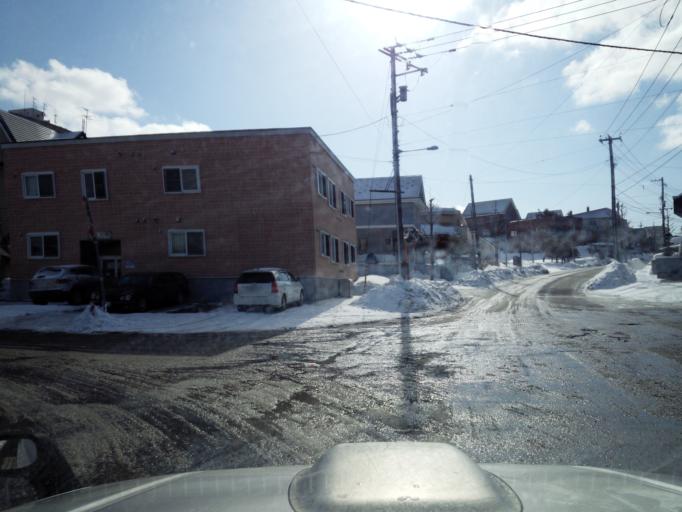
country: JP
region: Hokkaido
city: Kitahiroshima
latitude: 42.9861
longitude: 141.4450
